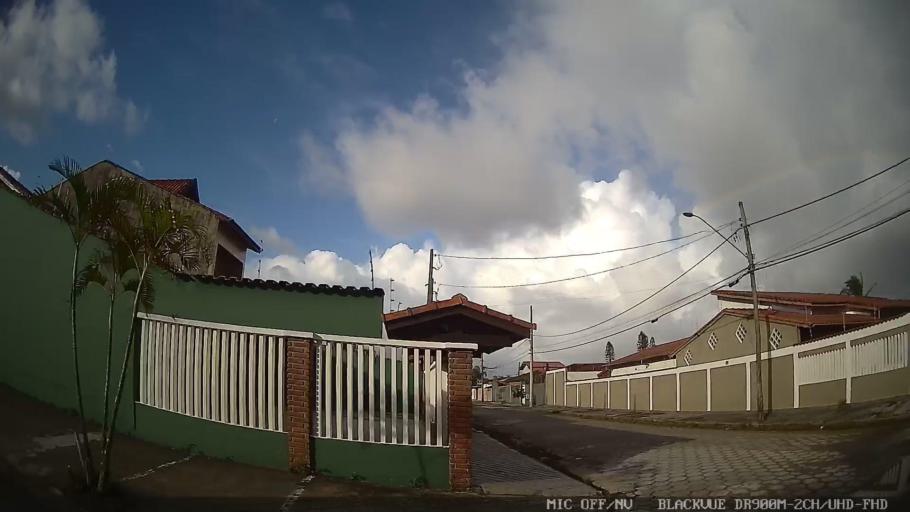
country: BR
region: Sao Paulo
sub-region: Itanhaem
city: Itanhaem
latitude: -24.2101
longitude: -46.8387
